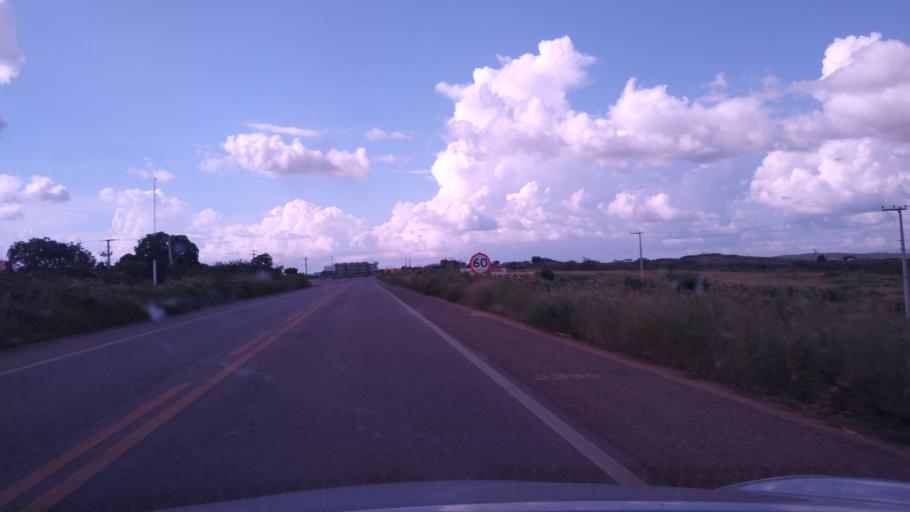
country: BR
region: Ceara
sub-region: Caninde
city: Caninde
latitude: -4.3882
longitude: -39.3129
